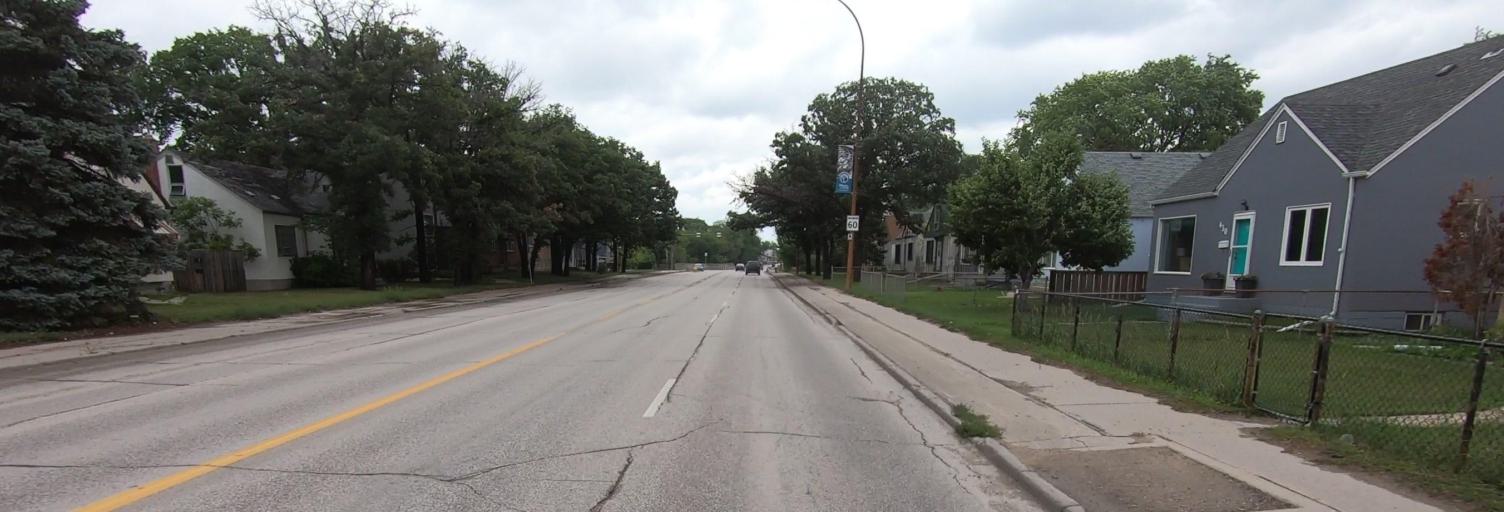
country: CA
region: Manitoba
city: Winnipeg
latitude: 49.8820
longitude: -97.1075
